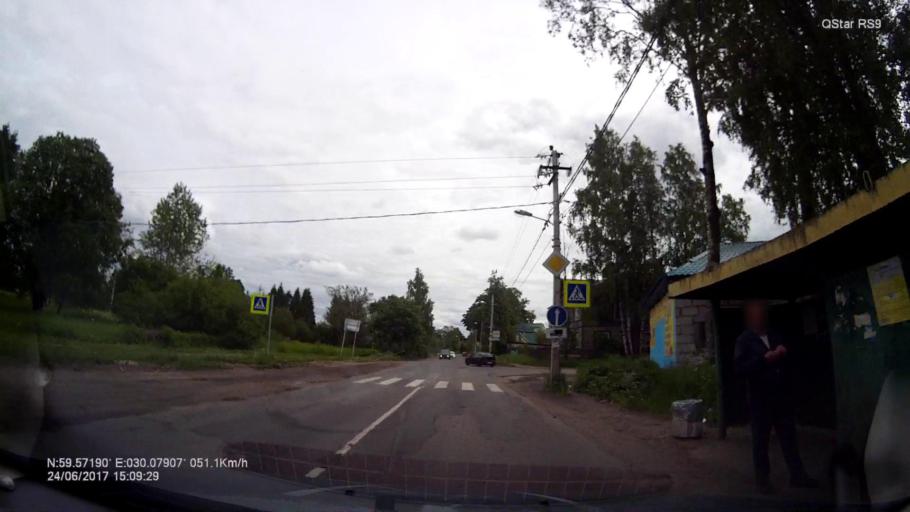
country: RU
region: Leningrad
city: Mariyenburg
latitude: 59.5718
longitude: 30.0793
